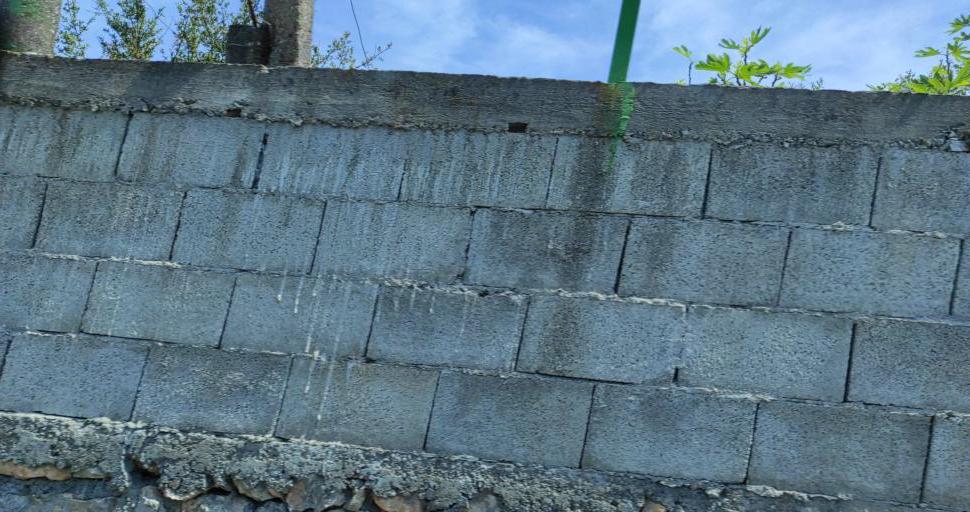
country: AL
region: Shkoder
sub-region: Rrethi i Malesia e Madhe
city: Gruemire
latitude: 42.1427
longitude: 19.5478
